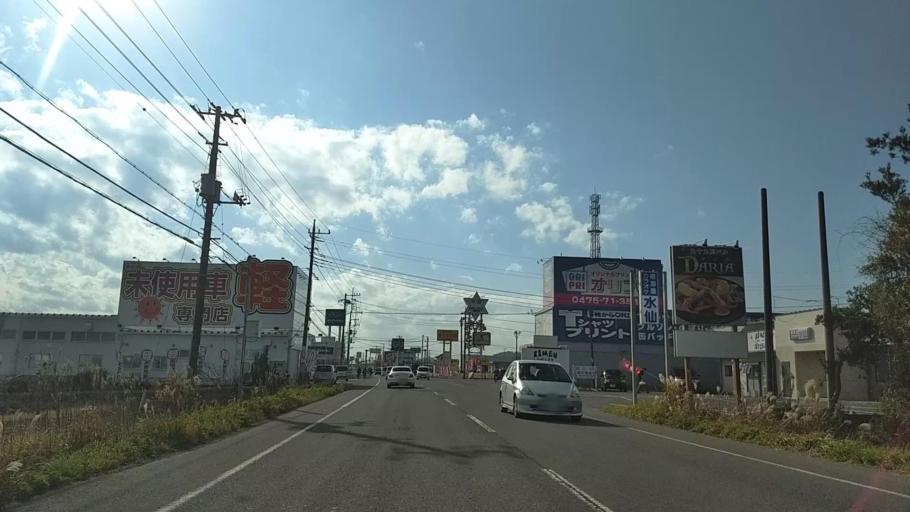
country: JP
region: Chiba
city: Naruto
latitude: 35.5889
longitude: 140.3921
